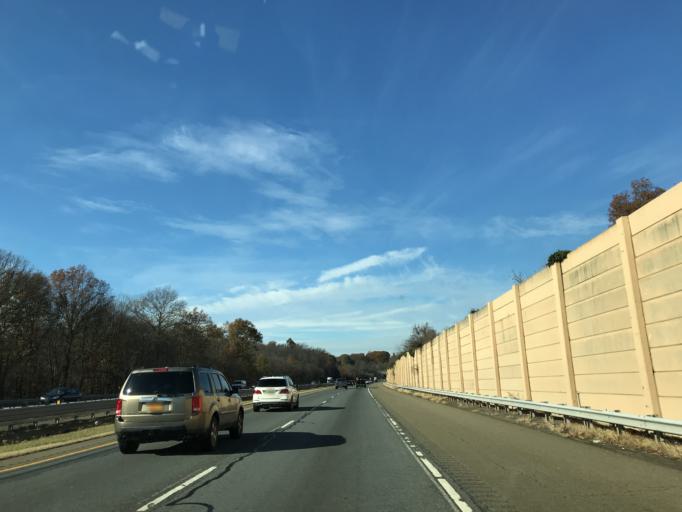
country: US
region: New Jersey
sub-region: Morris County
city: Madison
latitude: 40.7610
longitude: -74.3947
